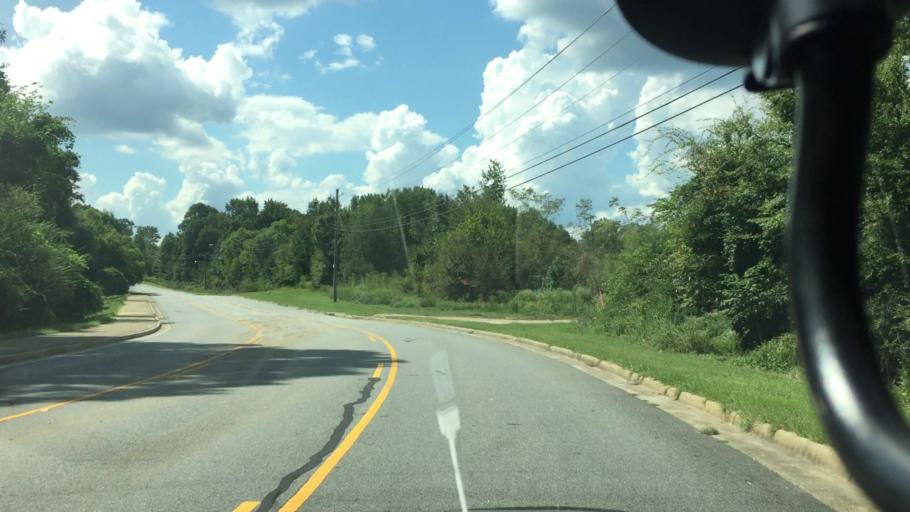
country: US
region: Alabama
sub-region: Lee County
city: Auburn
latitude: 32.5730
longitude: -85.5081
